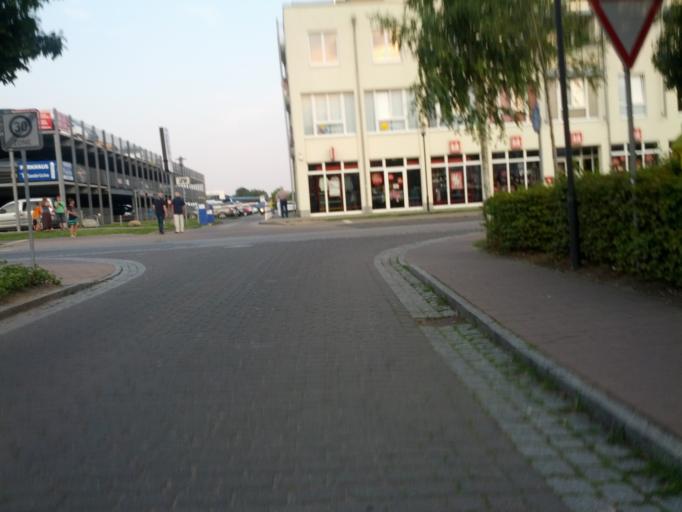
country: DE
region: Mecklenburg-Vorpommern
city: Ostseebad Kuhlungsborn
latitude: 54.1514
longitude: 11.7609
